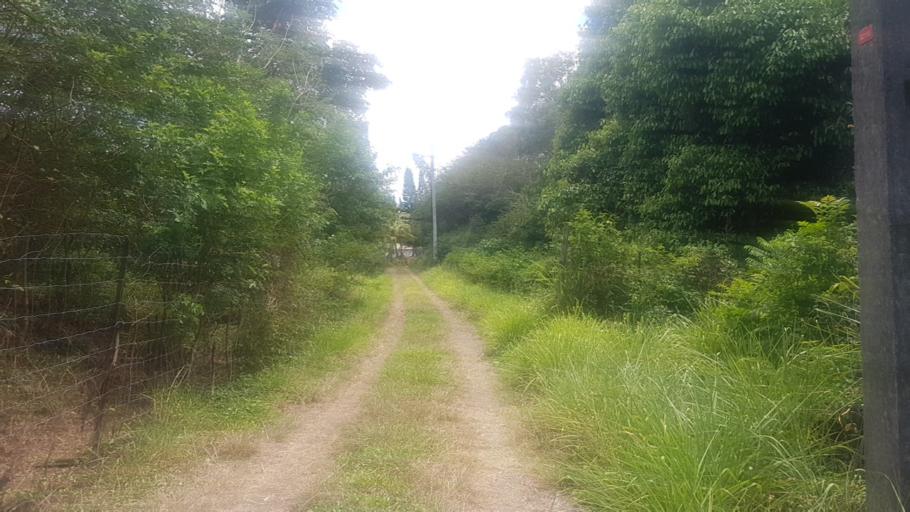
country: NC
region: South Province
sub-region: Dumbea
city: Dumbea
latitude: -22.1835
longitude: 166.4797
